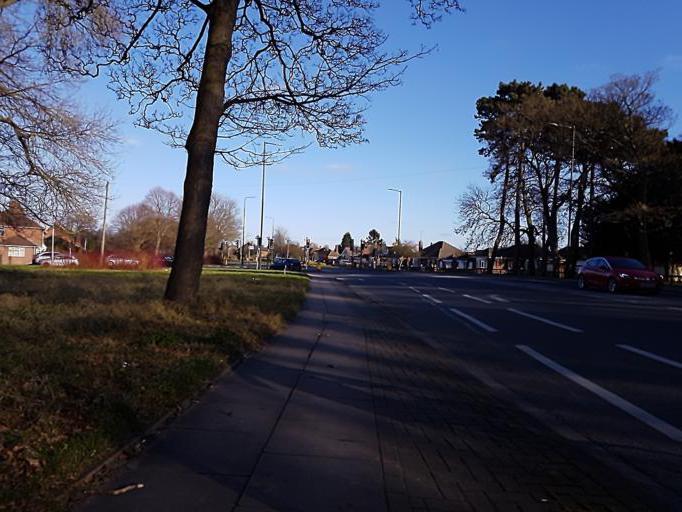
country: GB
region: England
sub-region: North East Lincolnshire
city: Grimsby
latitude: 53.5528
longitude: -0.0633
